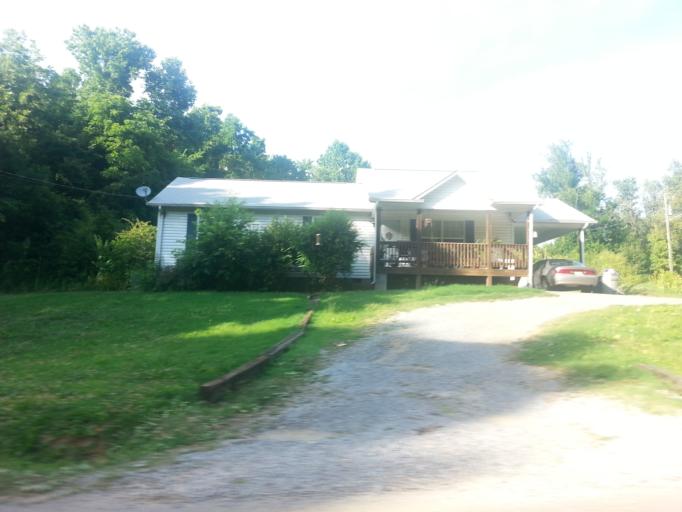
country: US
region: Tennessee
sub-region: Knox County
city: Knoxville
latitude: 35.9222
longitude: -83.9183
